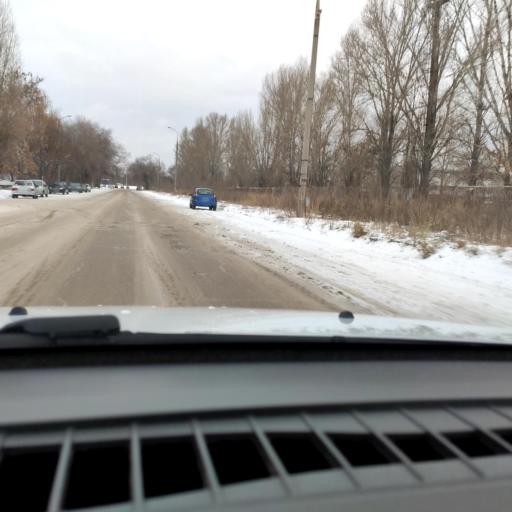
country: RU
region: Samara
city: Tol'yatti
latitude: 53.5554
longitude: 49.2998
